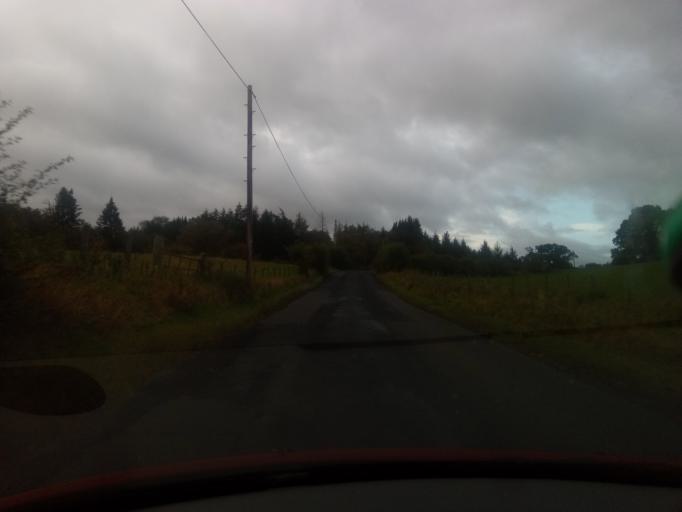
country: GB
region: Scotland
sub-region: The Scottish Borders
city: Jedburgh
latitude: 55.4544
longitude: -2.5593
